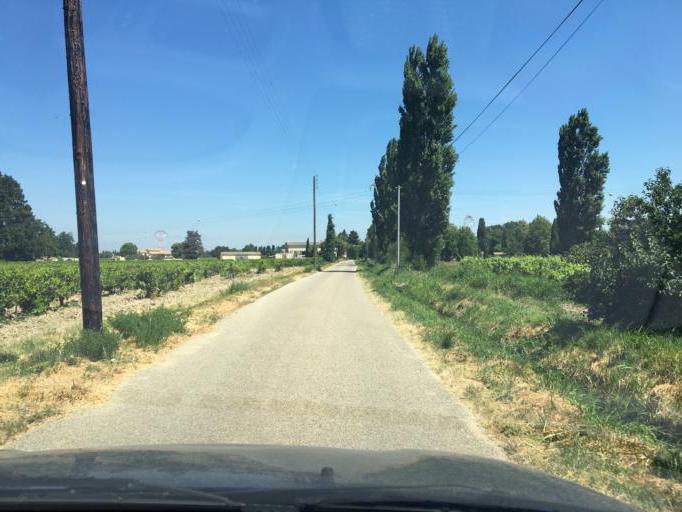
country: FR
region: Provence-Alpes-Cote d'Azur
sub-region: Departement du Vaucluse
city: Camaret-sur-Aigues
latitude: 44.1655
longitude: 4.8924
